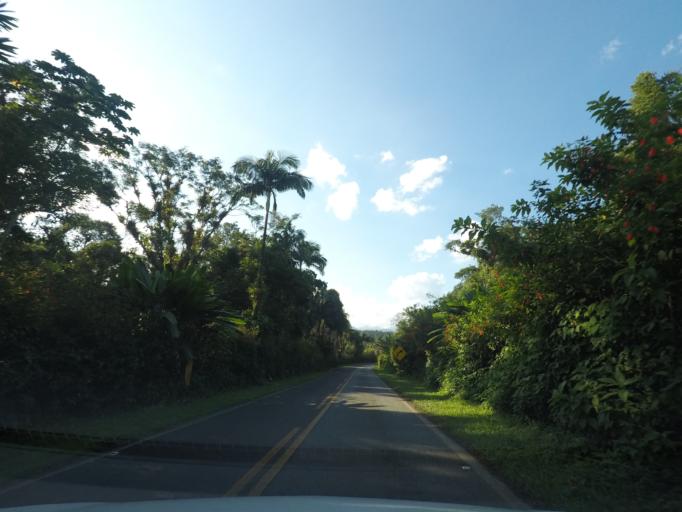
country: BR
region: Parana
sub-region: Antonina
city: Antonina
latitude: -25.4007
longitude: -48.8724
